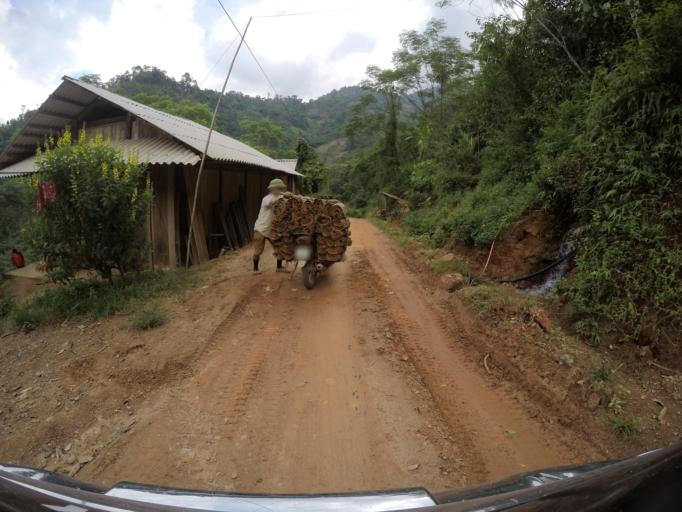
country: VN
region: Yen Bai
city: Son Thinh
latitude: 21.6798
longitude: 104.5823
